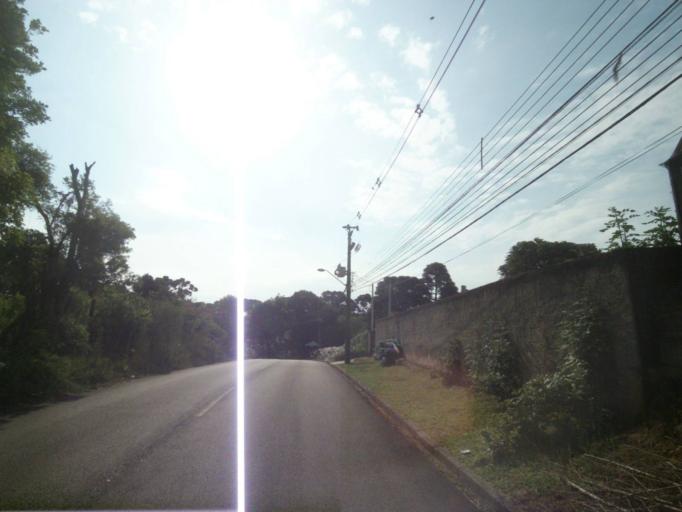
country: BR
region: Parana
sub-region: Curitiba
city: Curitiba
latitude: -25.4081
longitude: -49.3144
